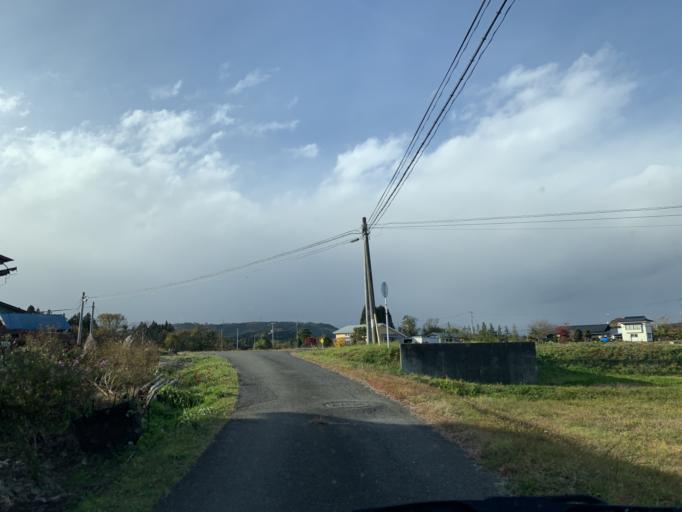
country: JP
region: Iwate
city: Ichinoseki
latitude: 39.0103
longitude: 141.0976
